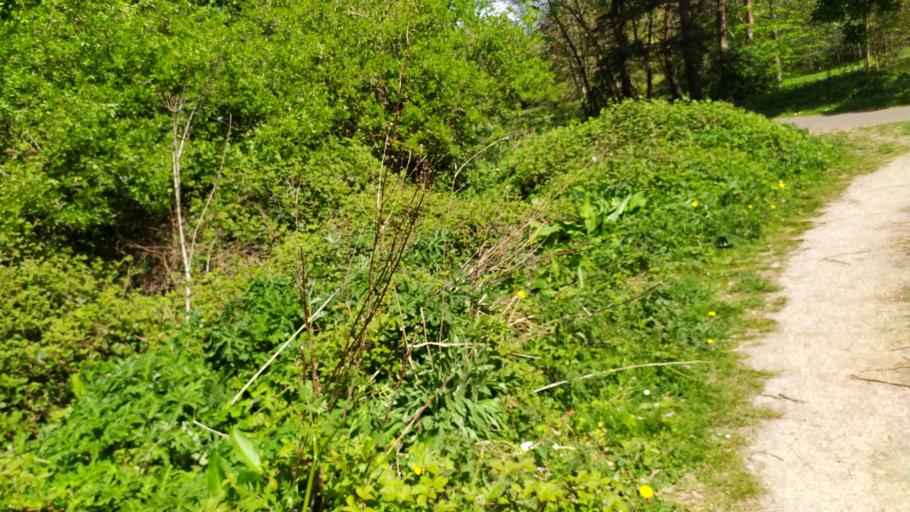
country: GB
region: England
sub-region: City and Borough of Leeds
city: Shadwell
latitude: 53.8059
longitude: -1.4826
